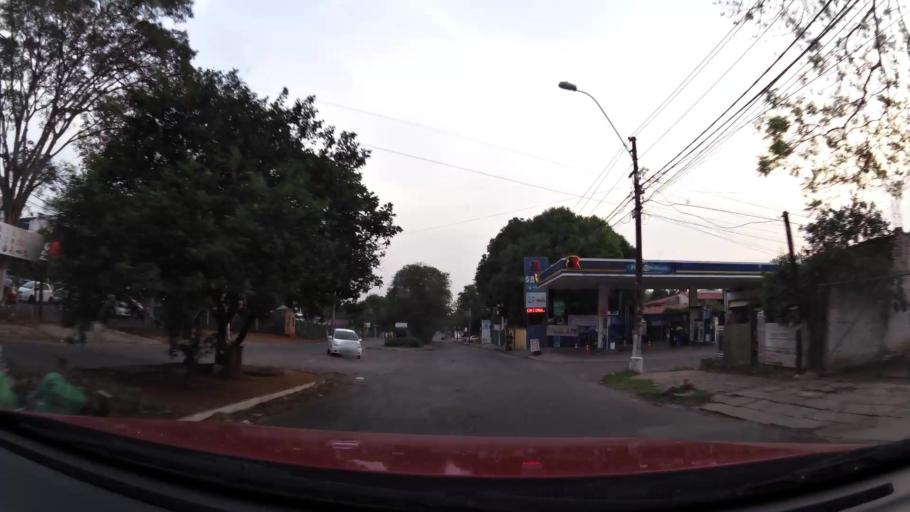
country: PY
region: Asuncion
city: Asuncion
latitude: -25.3166
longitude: -57.6130
